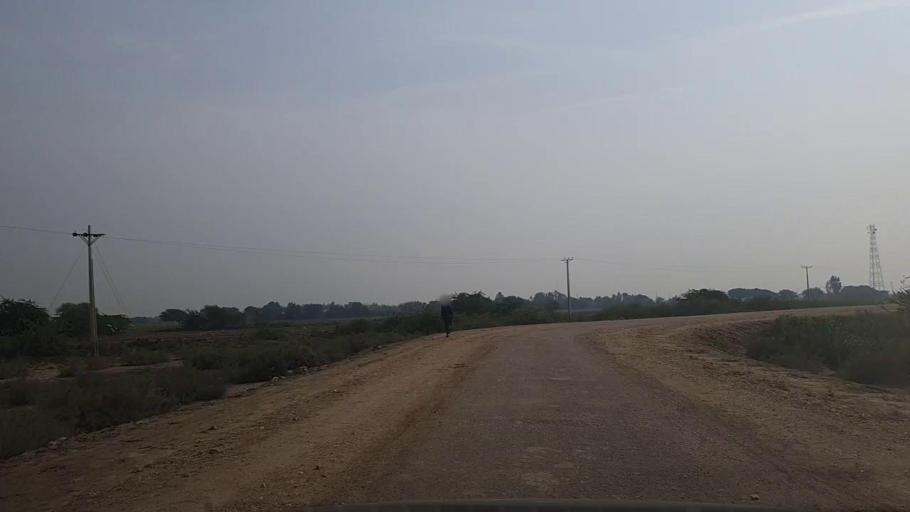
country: PK
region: Sindh
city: Mirpur Sakro
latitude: 24.4092
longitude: 67.7441
